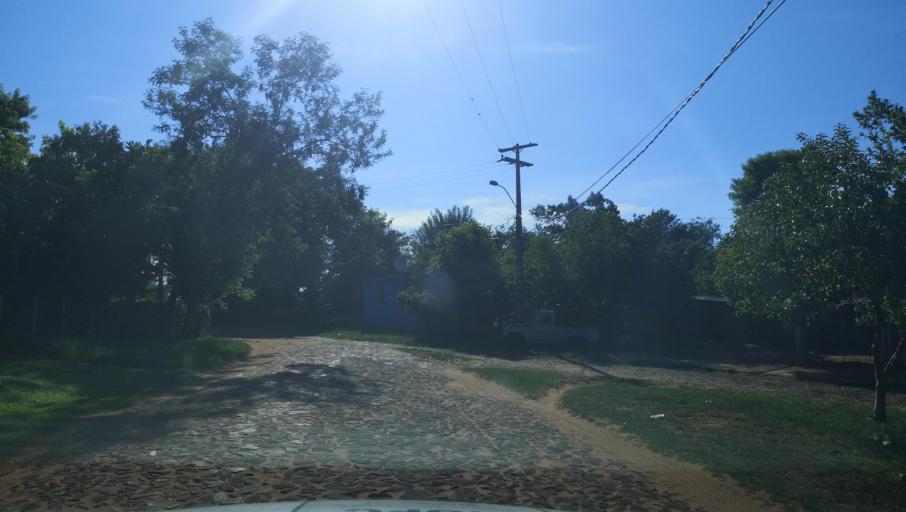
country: PY
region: Misiones
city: Santa Maria
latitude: -26.8818
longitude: -57.0085
